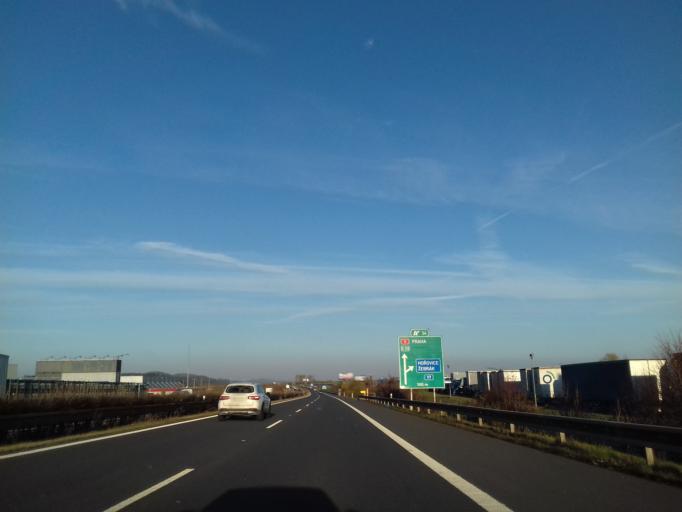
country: CZ
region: Central Bohemia
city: Zebrak
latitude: 49.8628
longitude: 13.8886
